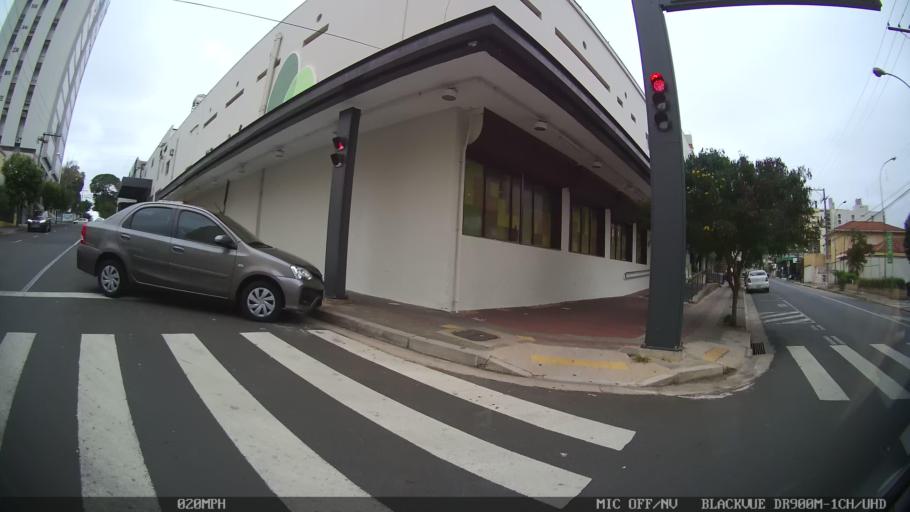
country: BR
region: Sao Paulo
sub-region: Sao Jose Do Rio Preto
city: Sao Jose do Rio Preto
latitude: -20.8154
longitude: -49.3865
